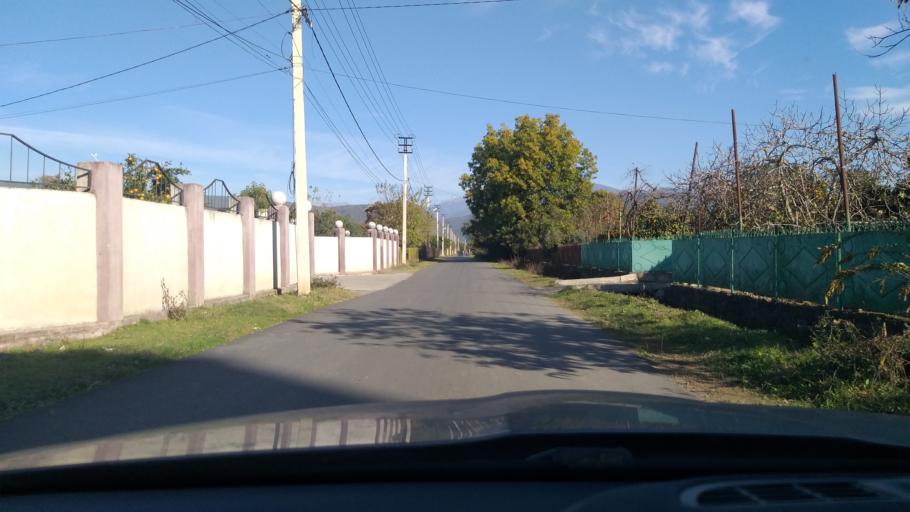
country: GE
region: Abkhazia
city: Sokhumi
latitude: 43.0152
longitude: 40.9639
